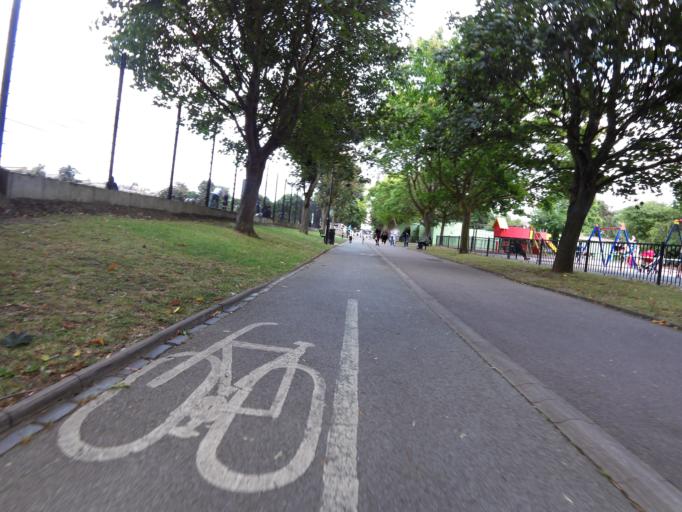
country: GB
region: England
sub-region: Greater London
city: Holloway
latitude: 51.5618
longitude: -0.1290
